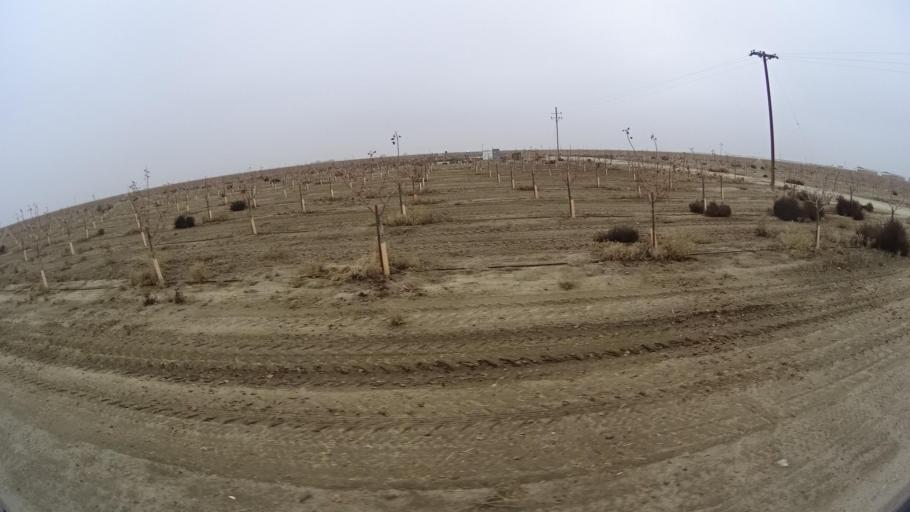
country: US
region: California
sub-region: Kern County
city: Wasco
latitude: 35.7064
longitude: -119.4195
